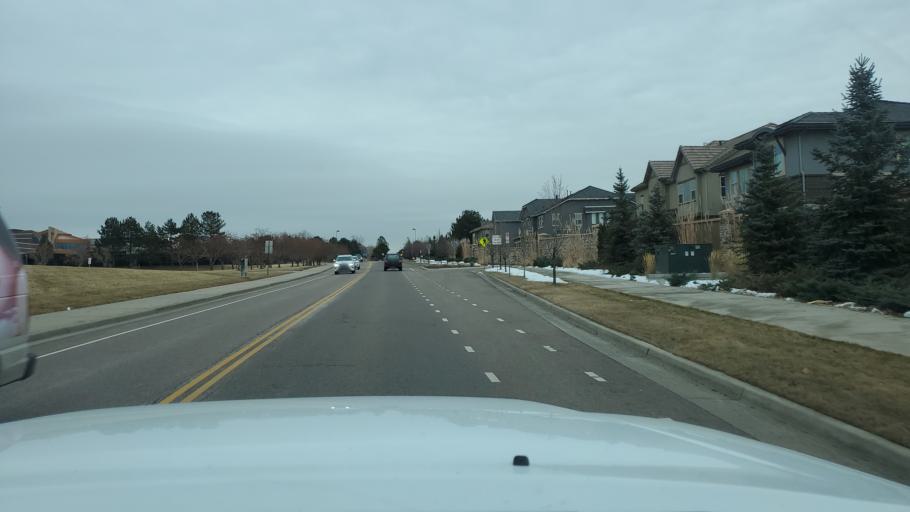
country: US
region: Colorado
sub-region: Arapahoe County
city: Castlewood
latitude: 39.6095
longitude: -104.9086
